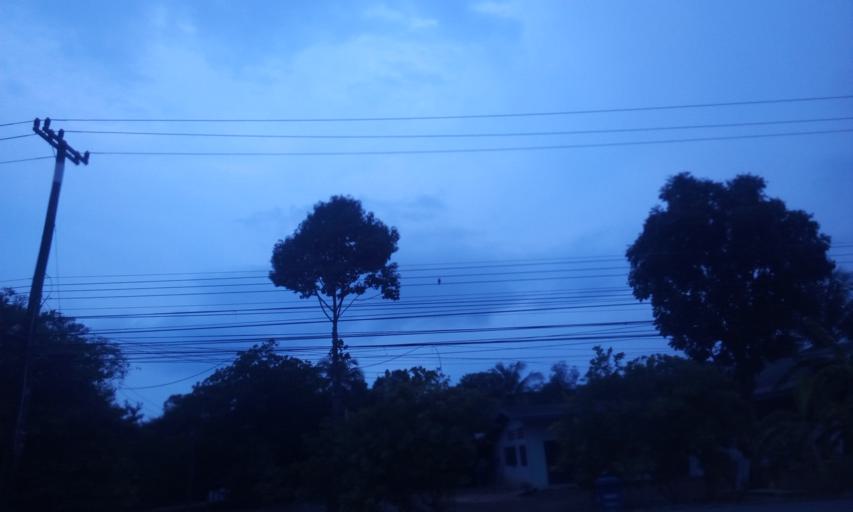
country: TH
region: Chanthaburi
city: Khlung
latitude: 12.4124
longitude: 102.3302
